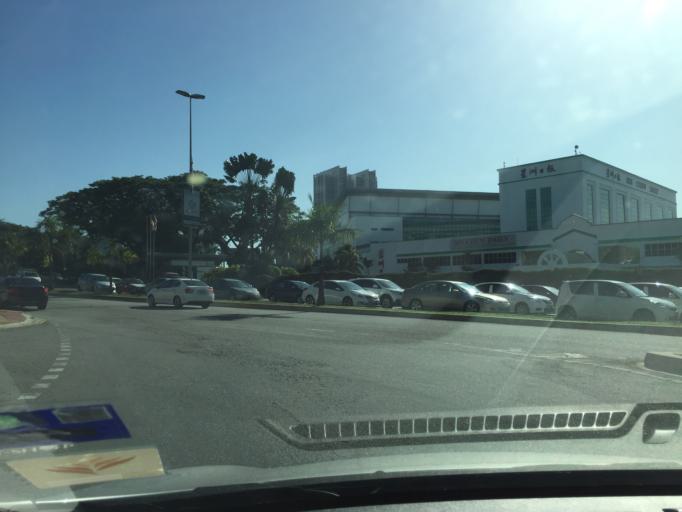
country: MY
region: Selangor
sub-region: Petaling
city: Petaling Jaya
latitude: 3.1176
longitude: 101.6299
